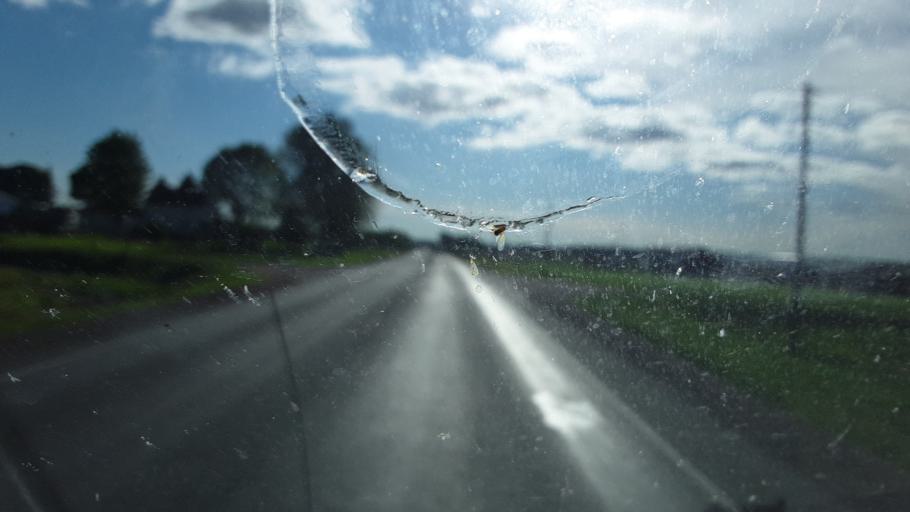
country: US
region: Wisconsin
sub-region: Marathon County
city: Spencer
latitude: 44.6562
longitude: -90.3361
